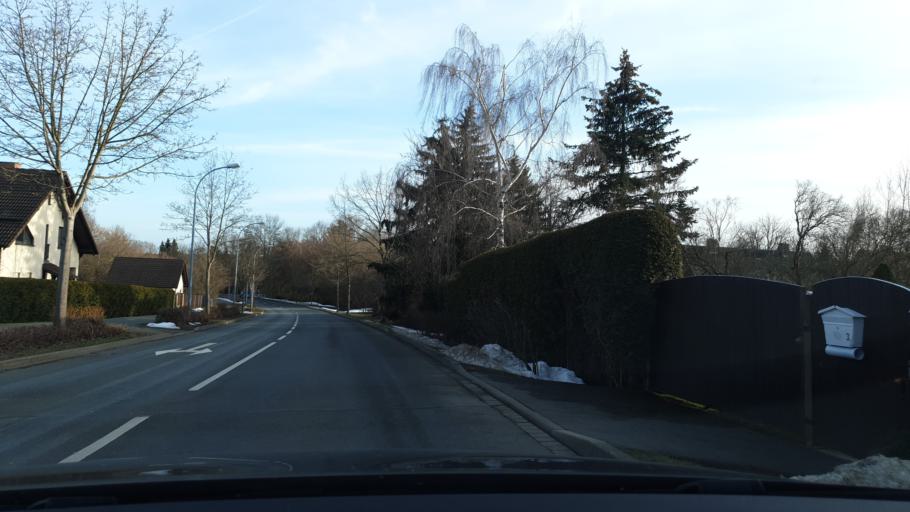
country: DE
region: Thuringia
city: Zeulenroda
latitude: 50.6442
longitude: 11.9781
